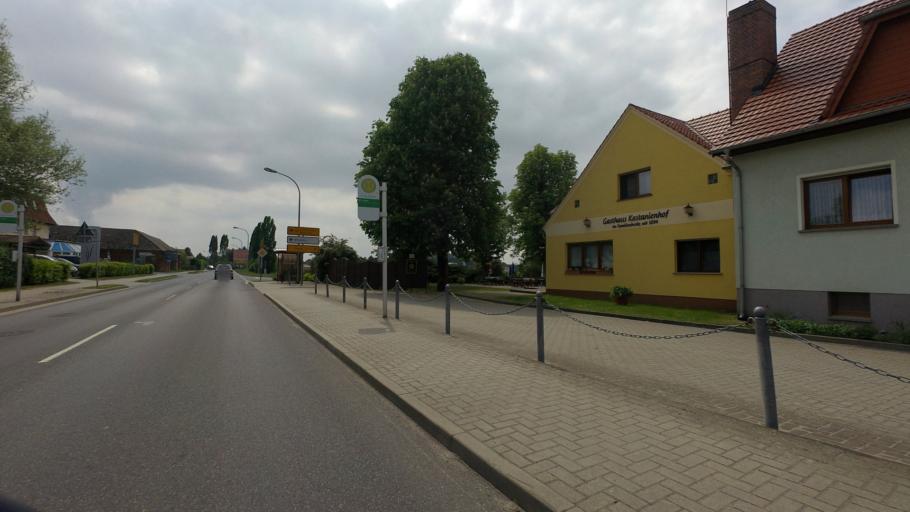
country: DE
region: Brandenburg
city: Drehnow
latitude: 51.8704
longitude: 14.3803
